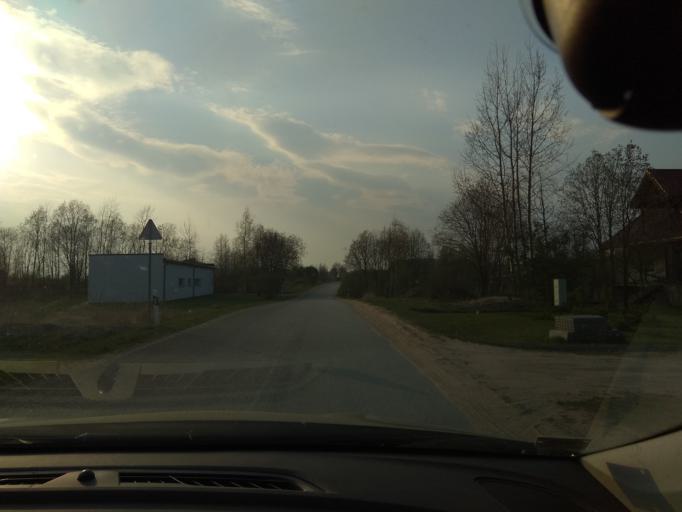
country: LT
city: Baltoji Voke
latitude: 54.5933
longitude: 25.1553
